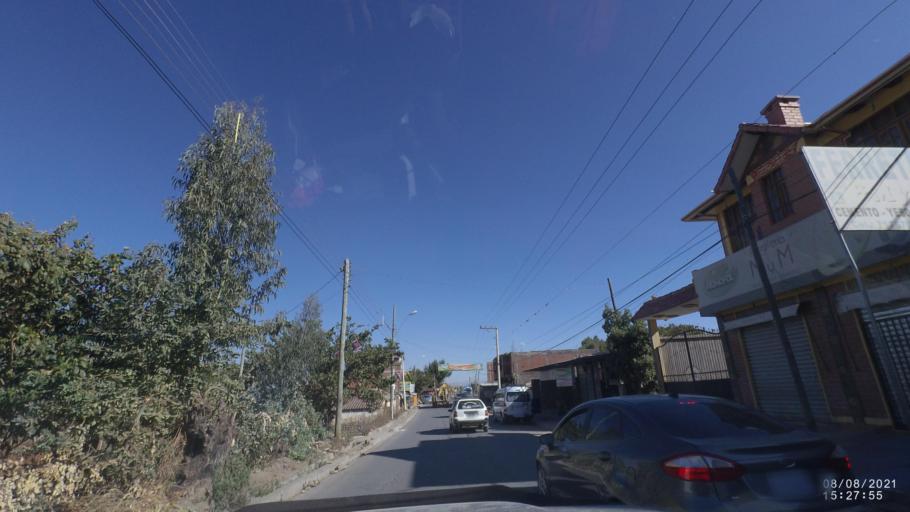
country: BO
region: Cochabamba
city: Cochabamba
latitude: -17.3309
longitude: -66.2829
